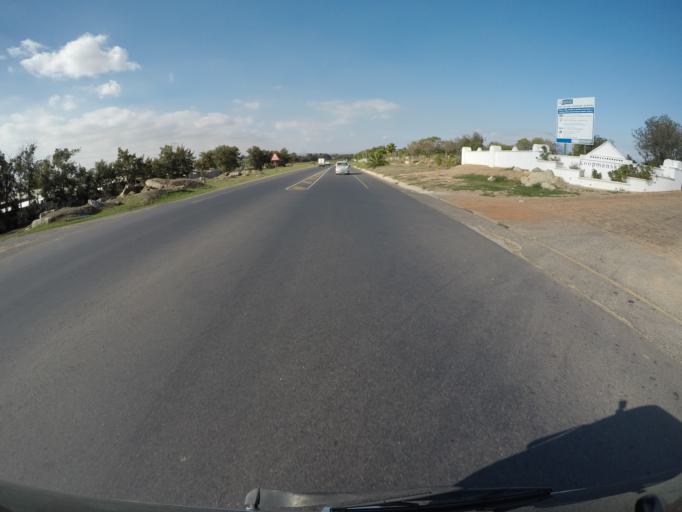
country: ZA
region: Western Cape
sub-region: City of Cape Town
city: Kraaifontein
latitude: -33.8868
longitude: 18.7472
